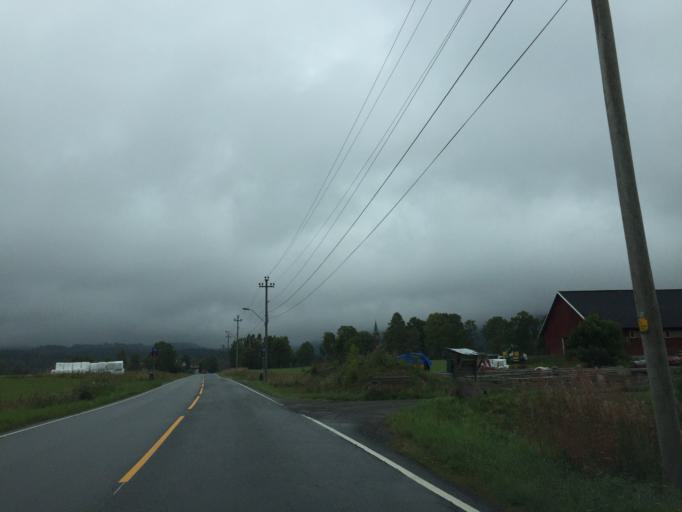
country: NO
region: Akershus
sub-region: Baerum
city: Lysaker
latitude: 60.0125
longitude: 10.6165
